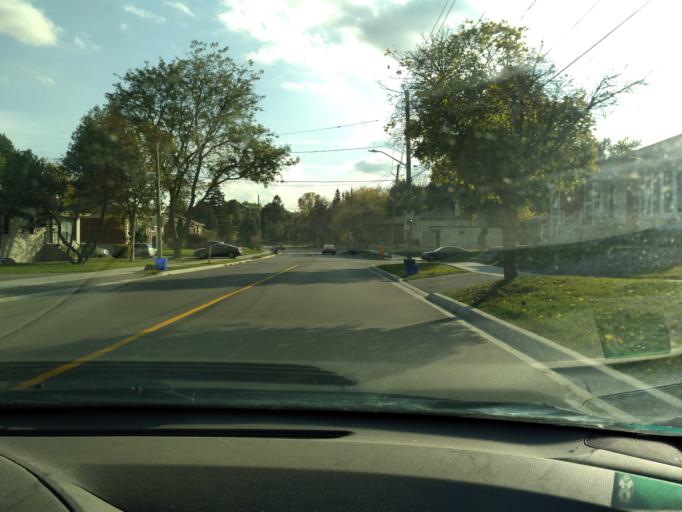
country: CA
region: Ontario
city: Newmarket
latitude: 44.0528
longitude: -79.4740
